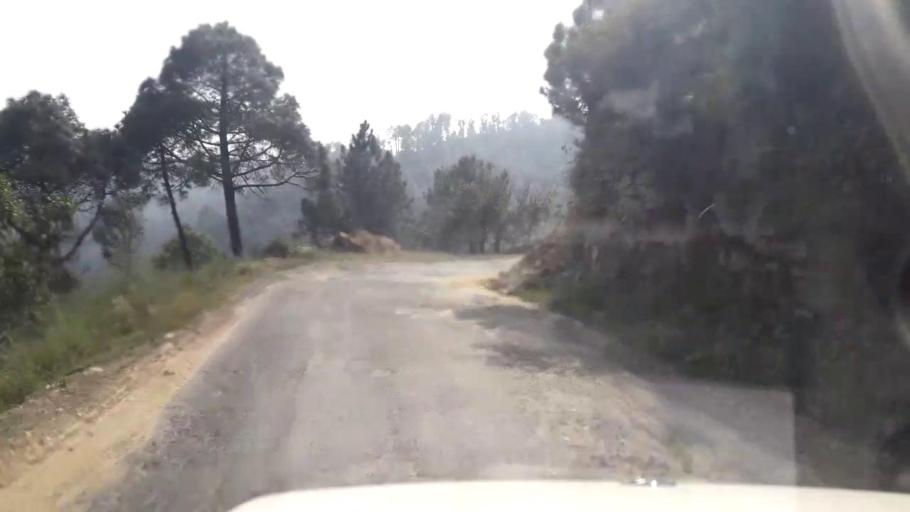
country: IN
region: Himachal Pradesh
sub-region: Shimla
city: Shimla
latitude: 31.0511
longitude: 77.1538
